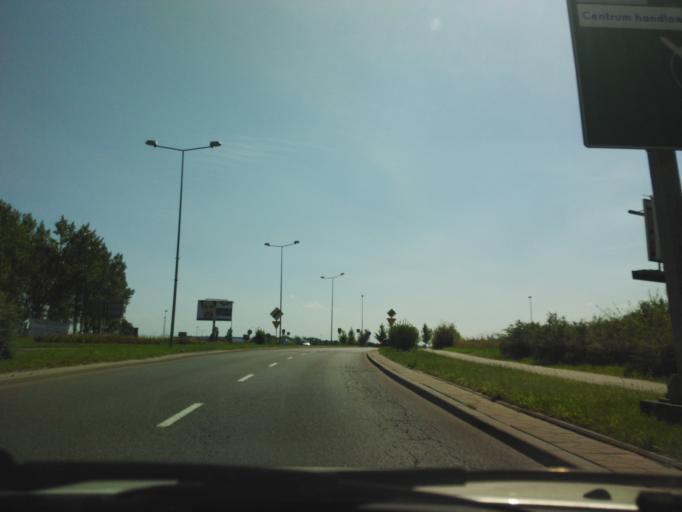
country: PL
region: West Pomeranian Voivodeship
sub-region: Powiat policki
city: Przeclaw
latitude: 53.3934
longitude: 14.5027
